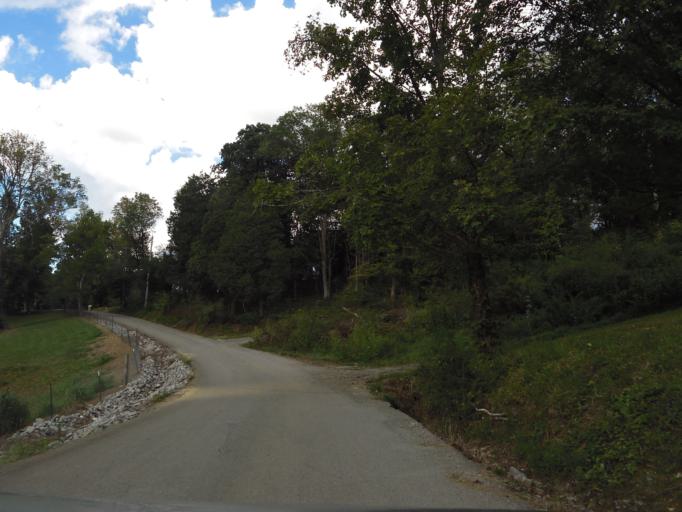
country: US
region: Tennessee
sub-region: Knox County
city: Mascot
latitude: 36.1164
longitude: -83.7767
